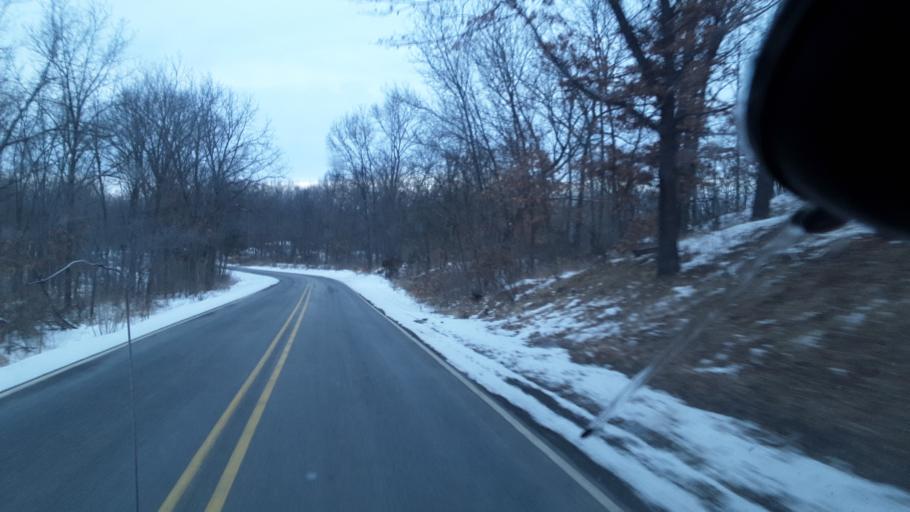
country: US
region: Michigan
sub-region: Ingham County
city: Leslie
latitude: 42.4443
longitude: -84.3243
